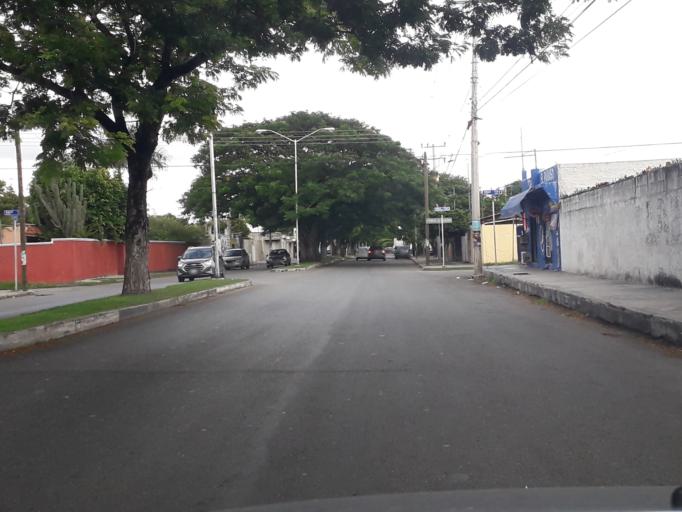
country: MX
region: Yucatan
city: Merida
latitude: 20.9625
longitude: -89.6581
